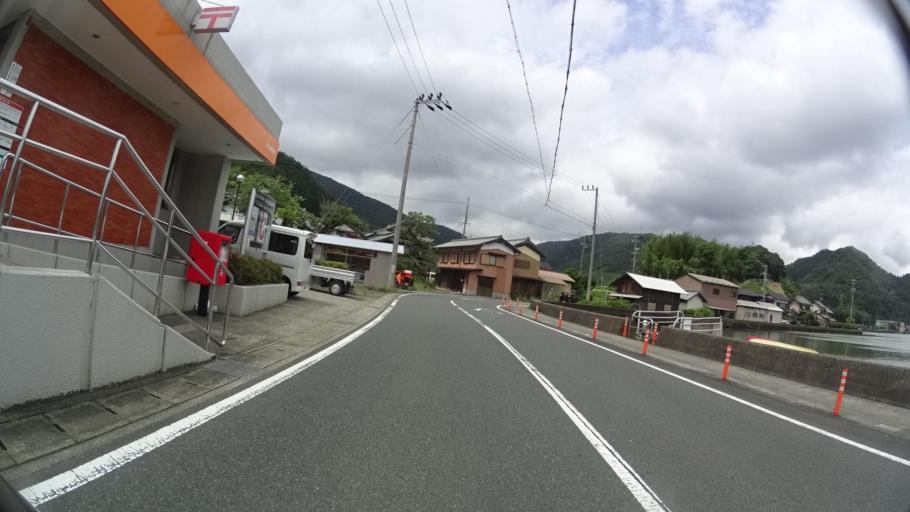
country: JP
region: Kyoto
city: Maizuru
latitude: 35.5160
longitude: 135.3887
